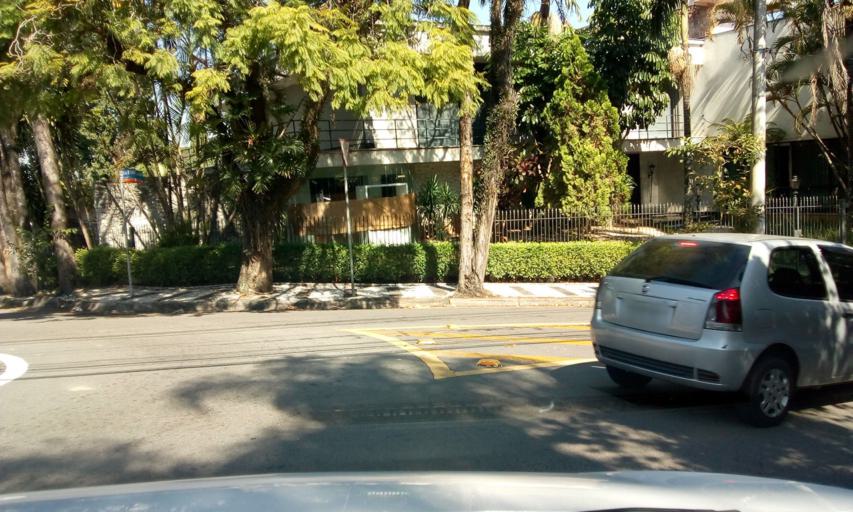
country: BR
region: Sao Paulo
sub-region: Taboao Da Serra
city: Taboao da Serra
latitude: -23.5979
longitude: -46.7097
